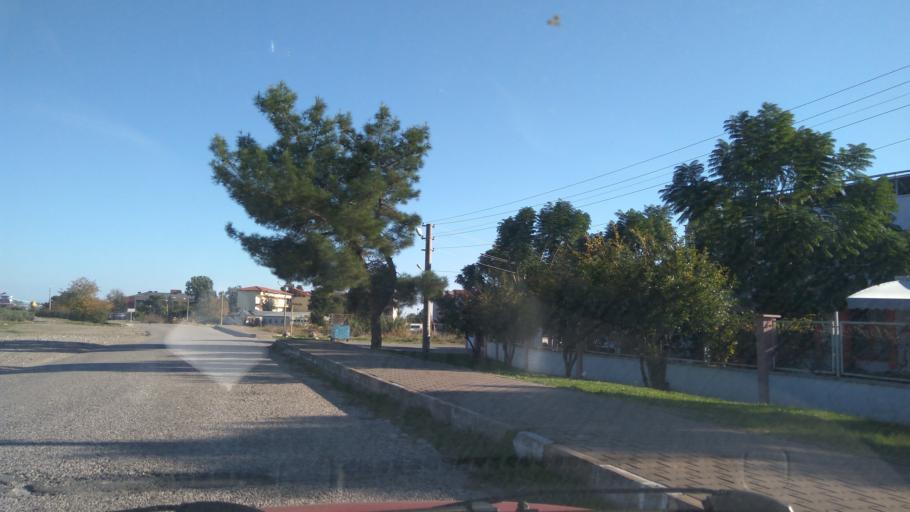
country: TR
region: Antalya
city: Kemer
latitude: 36.5674
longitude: 30.5635
